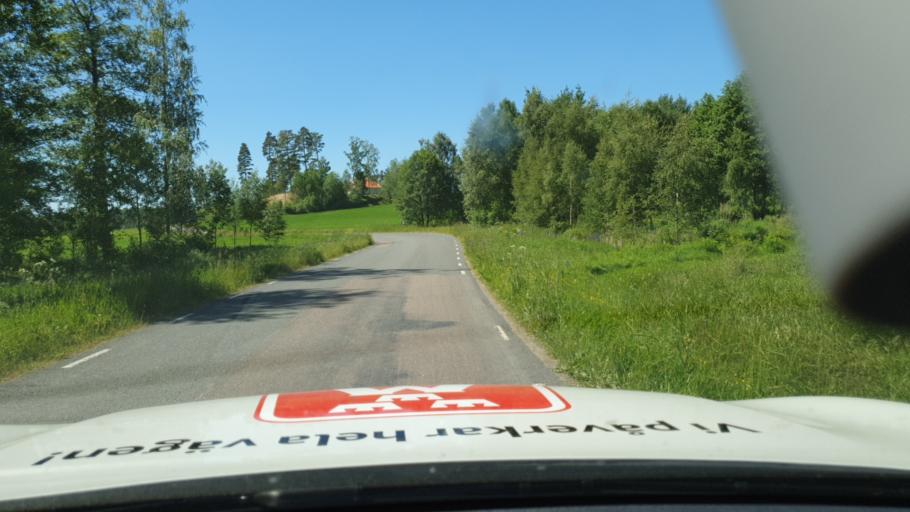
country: SE
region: Joenkoeping
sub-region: Habo Kommun
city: Habo
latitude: 57.9602
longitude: 14.0545
